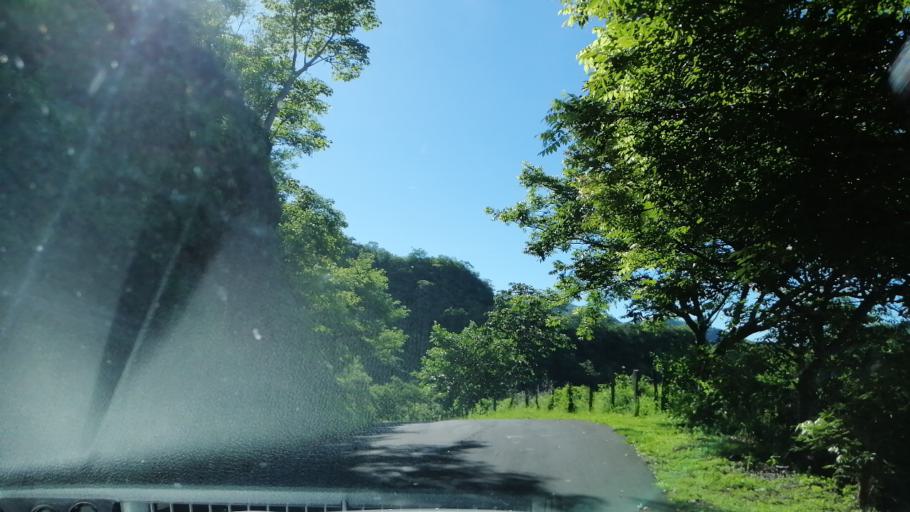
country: SV
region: Morazan
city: Corinto
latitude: 13.7905
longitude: -88.0178
